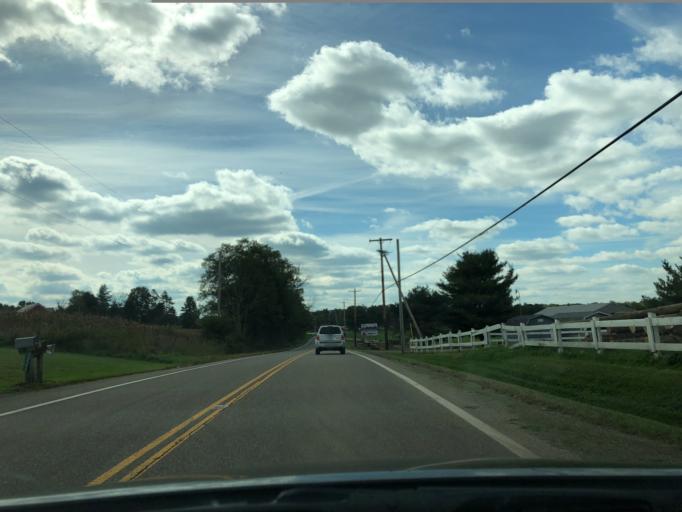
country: US
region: Ohio
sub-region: Stark County
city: Brewster
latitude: 40.6728
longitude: -81.6178
